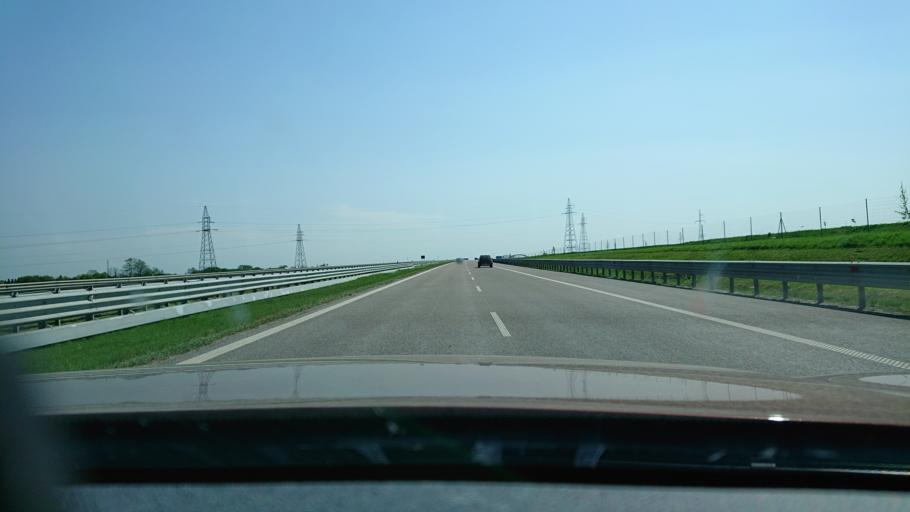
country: PL
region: Subcarpathian Voivodeship
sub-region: Powiat przemyski
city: Orly
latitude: 49.9149
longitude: 22.7845
